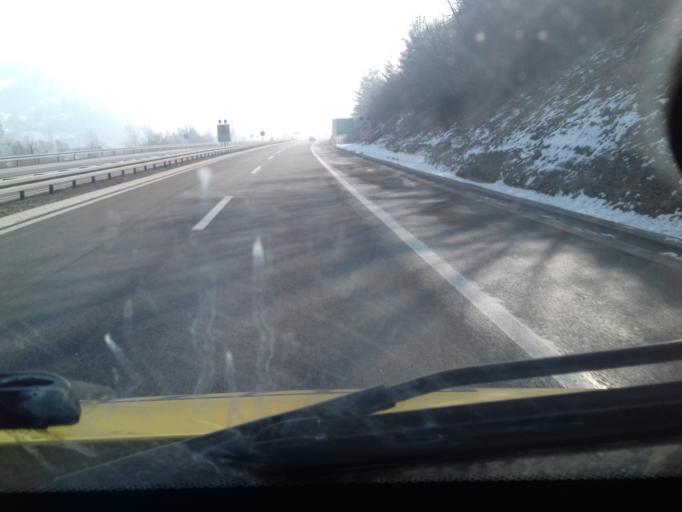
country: BA
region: Federation of Bosnia and Herzegovina
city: Vogosca
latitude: 43.9148
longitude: 18.3178
